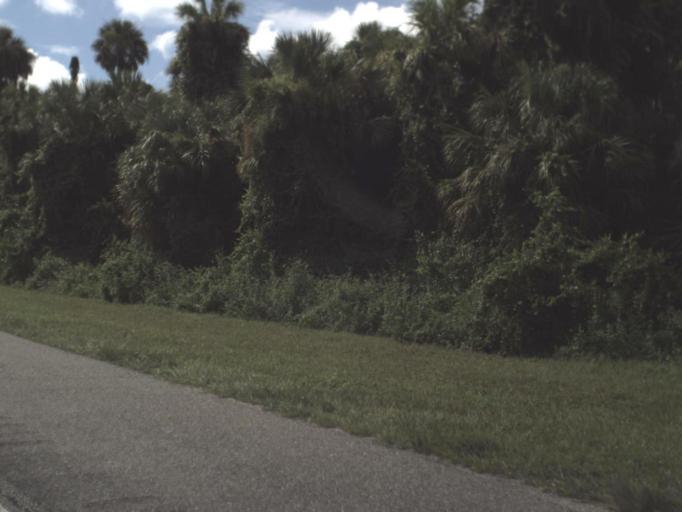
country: US
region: Florida
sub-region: Charlotte County
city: Port Charlotte
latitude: 27.0791
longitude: -82.1067
